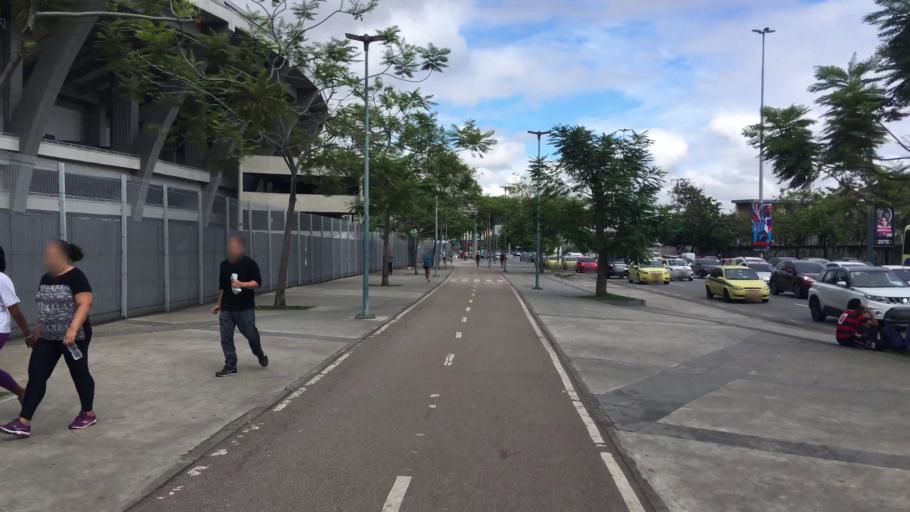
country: BR
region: Rio de Janeiro
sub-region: Rio De Janeiro
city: Rio de Janeiro
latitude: -22.9107
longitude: -43.2287
